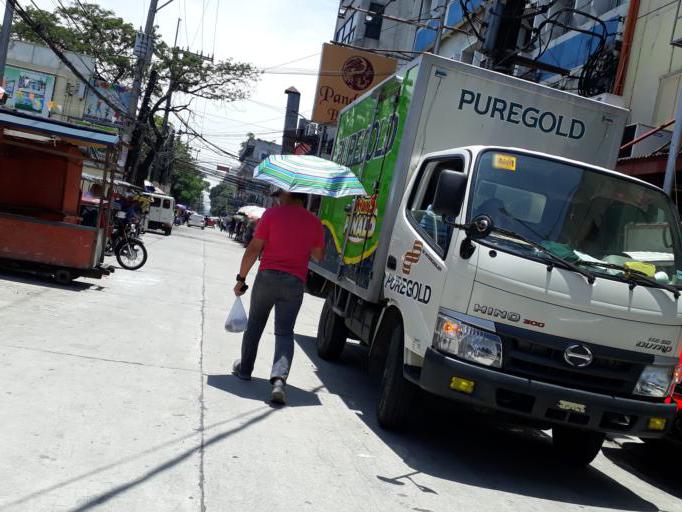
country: PH
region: Metro Manila
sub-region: Caloocan City
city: Niugan
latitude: 14.6535
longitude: 120.9848
